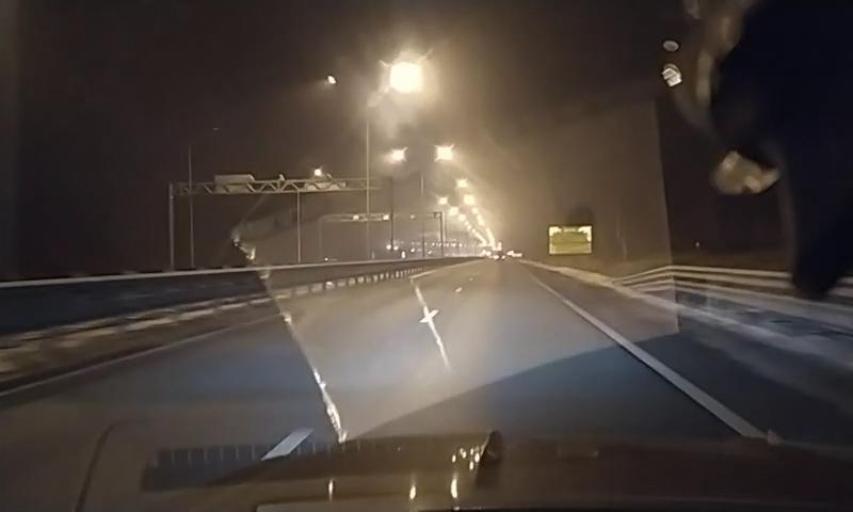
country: RU
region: Leningrad
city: Bugry
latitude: 60.1022
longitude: 30.3850
